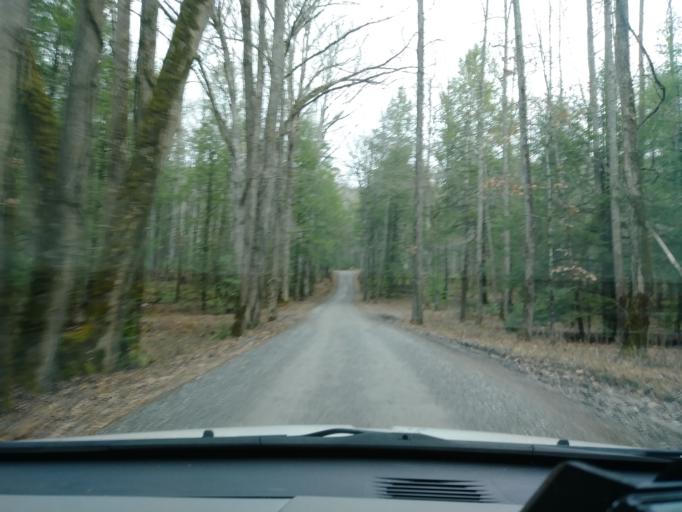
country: US
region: Tennessee
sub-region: Blount County
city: Wildwood
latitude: 35.6049
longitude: -83.8119
